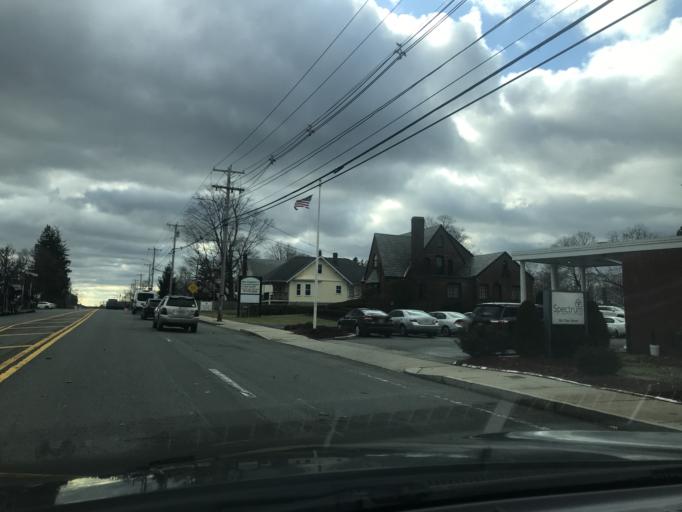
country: US
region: Massachusetts
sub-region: Norfolk County
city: Weymouth
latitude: 42.1758
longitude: -70.9554
